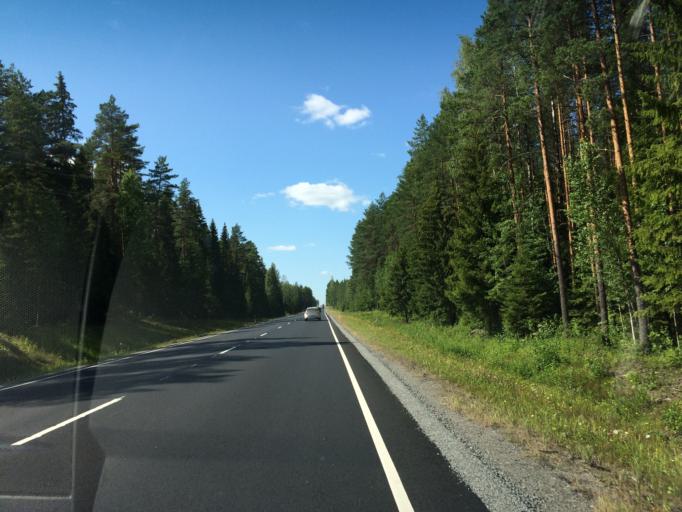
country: FI
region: Pirkanmaa
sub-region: Lounais-Pirkanmaa
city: Kiikoinen
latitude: 61.4737
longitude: 22.4980
